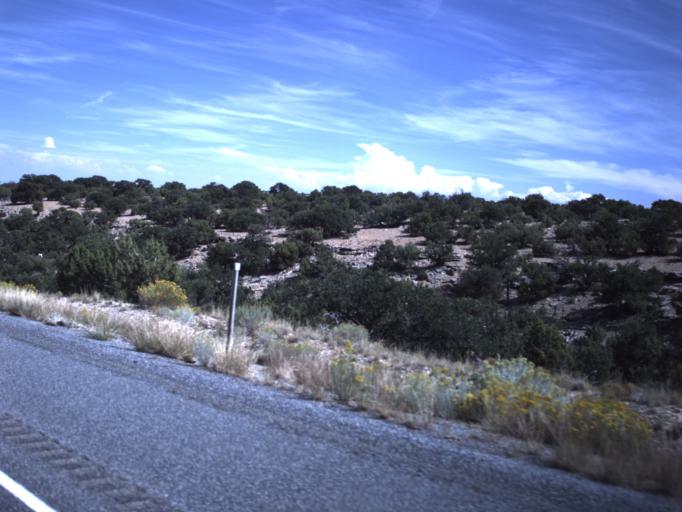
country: US
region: Utah
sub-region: Emery County
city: Castle Dale
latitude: 38.8985
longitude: -110.5750
